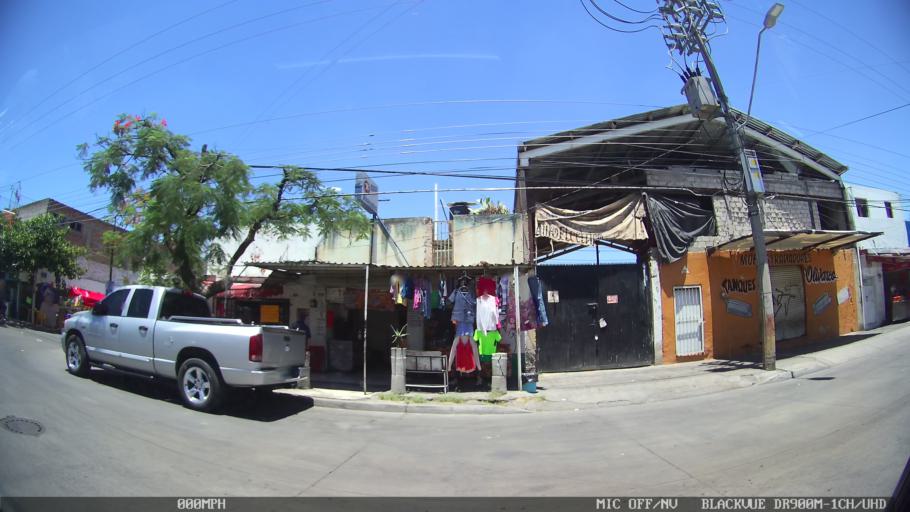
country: MX
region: Jalisco
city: Tlaquepaque
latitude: 20.6663
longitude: -103.2766
